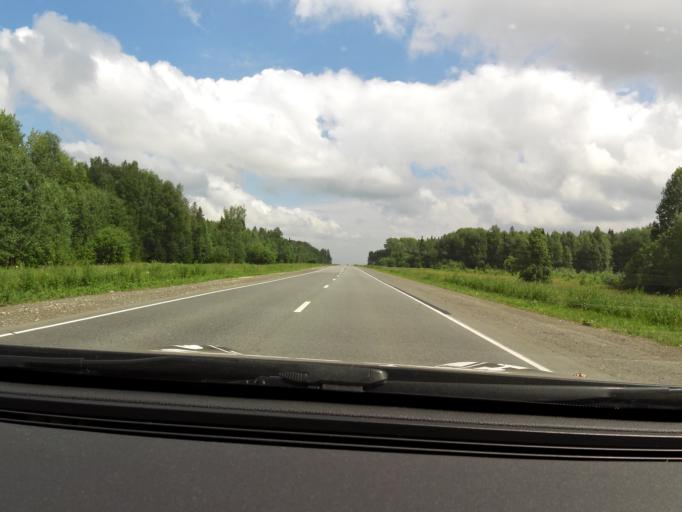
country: RU
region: Perm
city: Ust'-Kishert'
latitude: 57.1594
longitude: 57.1723
